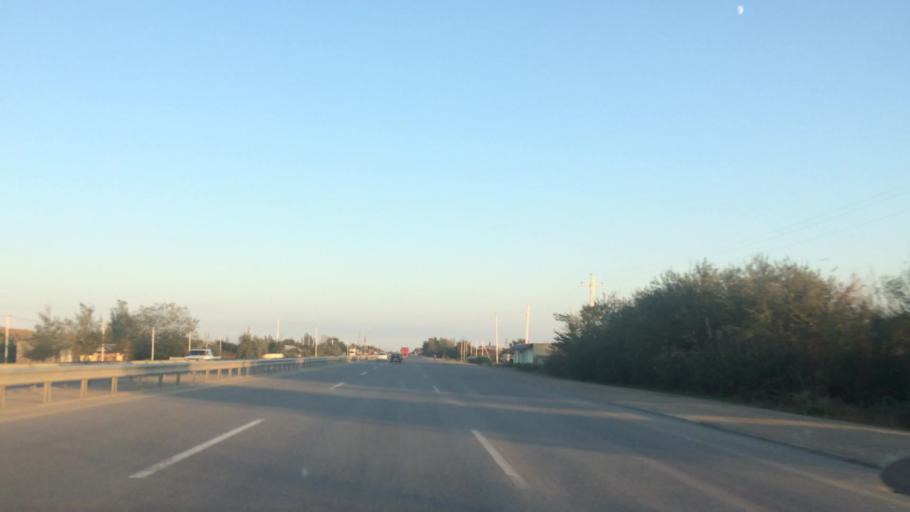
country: AZ
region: Haciqabul
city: Haciqabul
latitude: 40.0170
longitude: 49.1333
